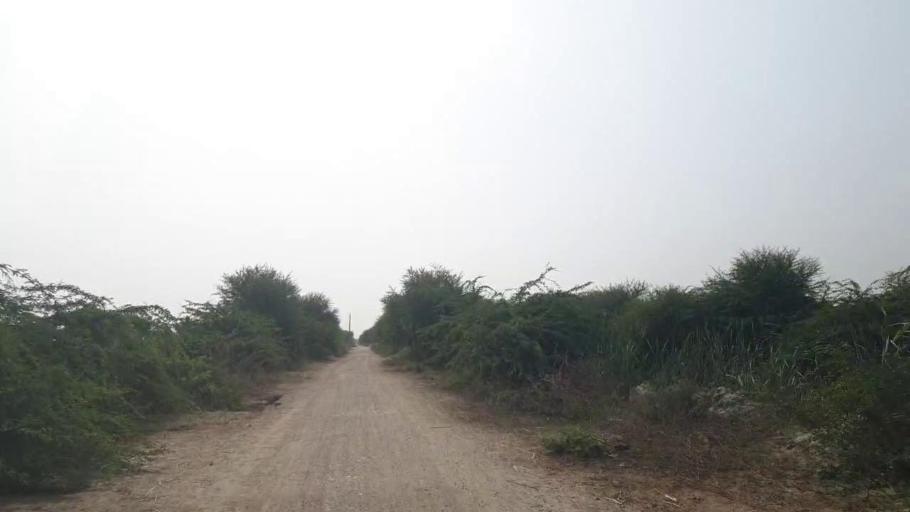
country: PK
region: Sindh
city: Badin
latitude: 24.6143
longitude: 68.7223
